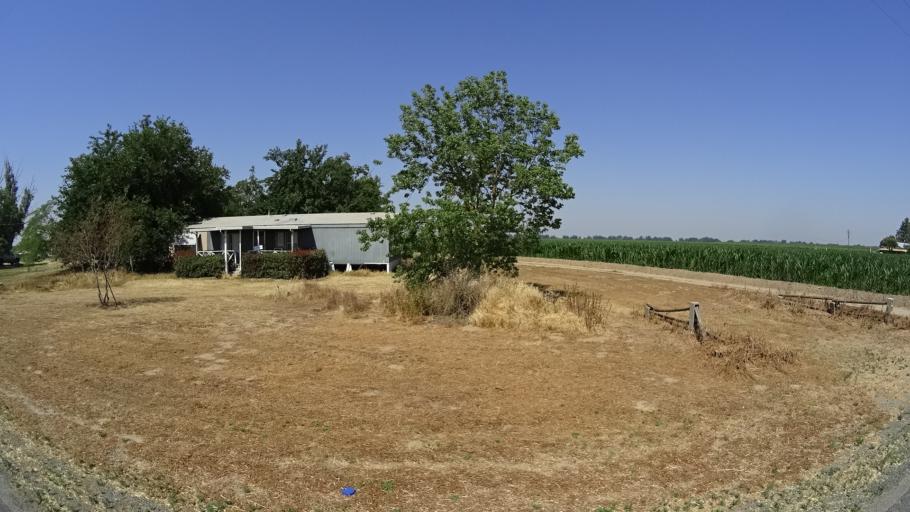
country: US
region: California
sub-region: Fresno County
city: Kingsburg
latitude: 36.4475
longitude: -119.5285
